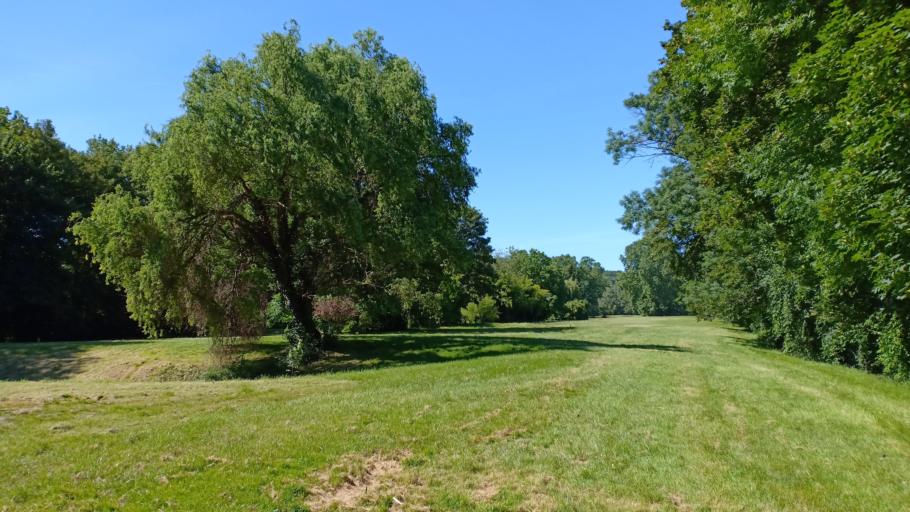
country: FR
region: Ile-de-France
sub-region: Departement des Yvelines
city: Croissy-sur-Seine
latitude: 48.8749
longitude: 2.1527
